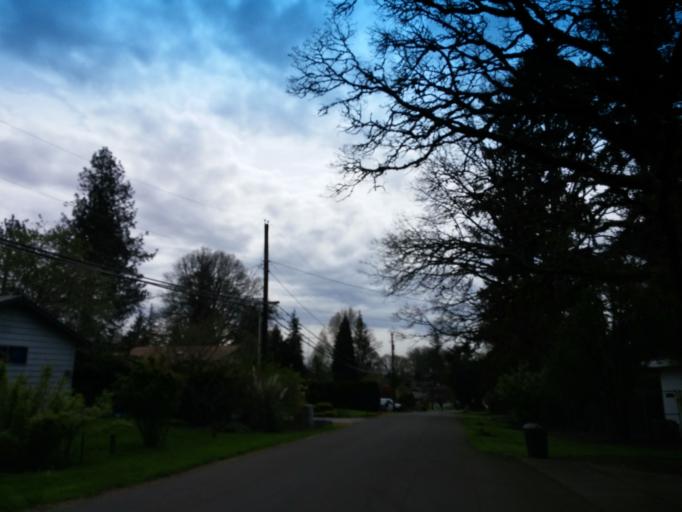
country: US
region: Oregon
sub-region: Washington County
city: Cedar Mill
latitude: 45.5280
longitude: -122.8111
